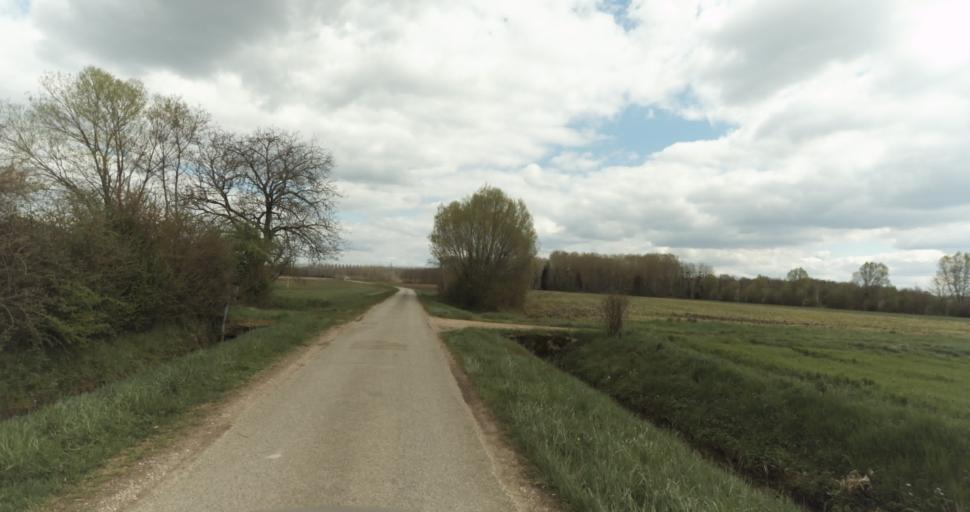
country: FR
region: Bourgogne
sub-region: Departement de la Cote-d'Or
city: Auxonne
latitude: 47.1591
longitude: 5.3868
